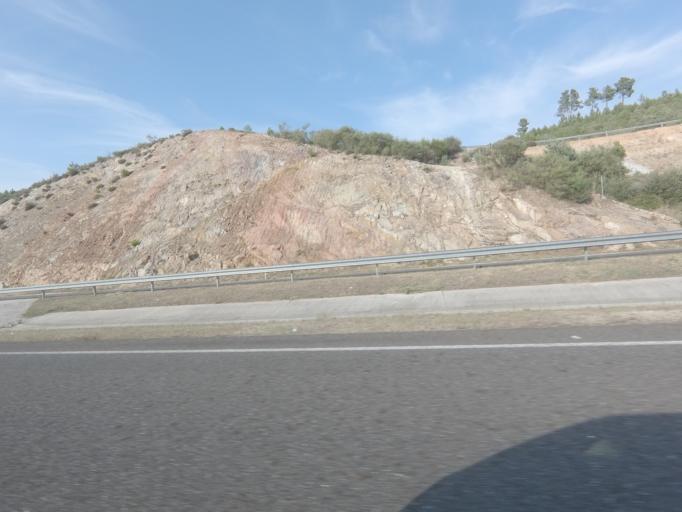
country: ES
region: Galicia
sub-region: Provincia de Ourense
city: Oimbra
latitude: 41.8580
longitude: -7.4247
